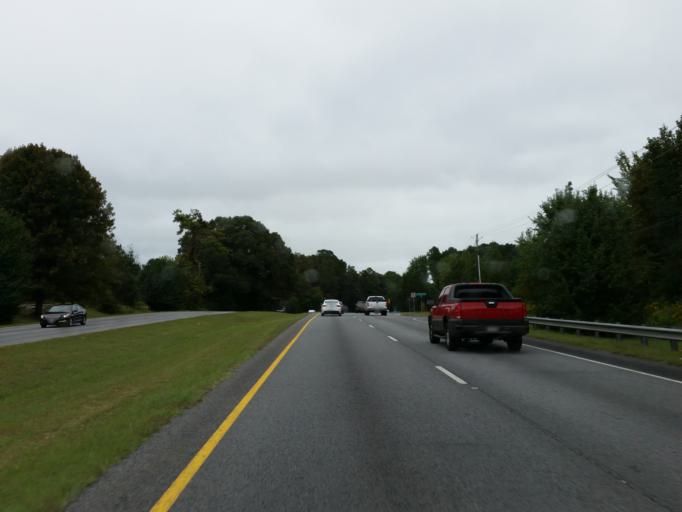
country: US
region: Georgia
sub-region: Clayton County
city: Bonanza
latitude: 33.4621
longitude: -84.3320
